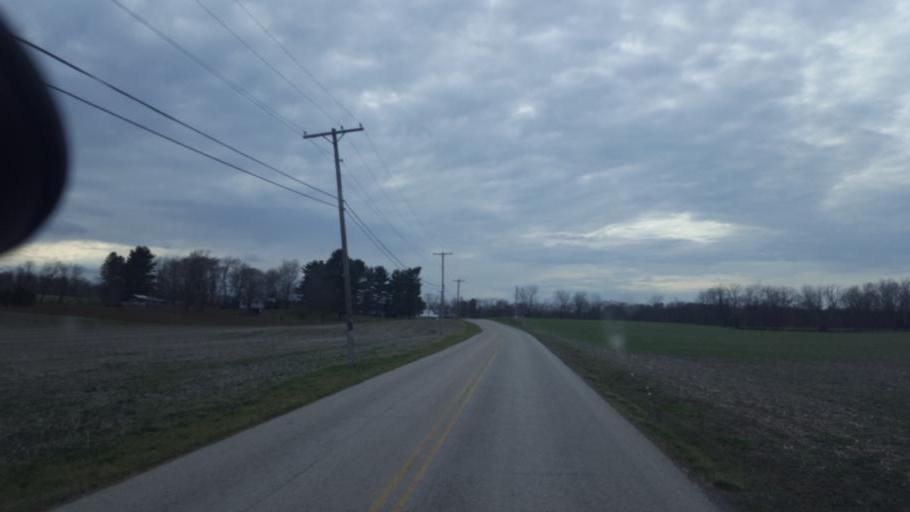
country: US
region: Ohio
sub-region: Richland County
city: Lexington
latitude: 40.6184
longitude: -82.5935
